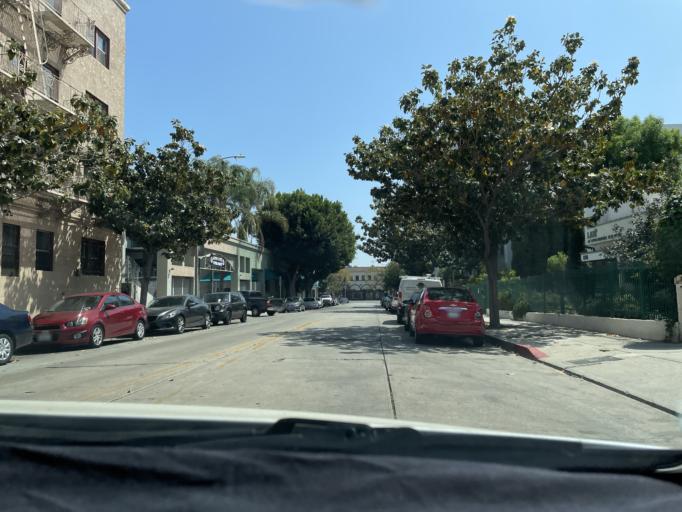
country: US
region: California
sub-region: Los Angeles County
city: Hollywood
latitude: 34.1030
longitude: -118.3348
